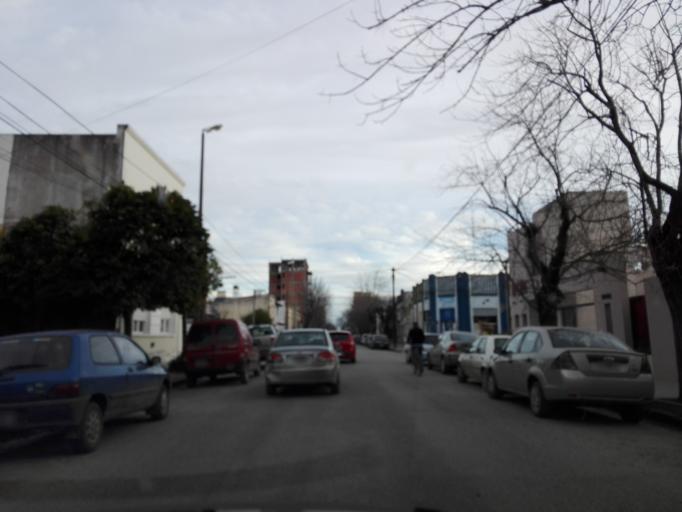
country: AR
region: Buenos Aires
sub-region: Partido de Balcarce
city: Balcarce
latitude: -37.8469
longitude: -58.2521
